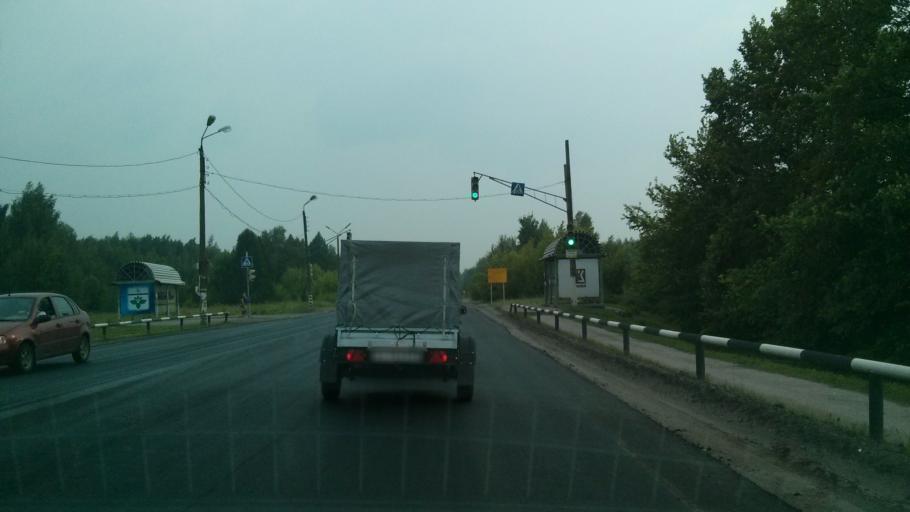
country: RU
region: Nizjnij Novgorod
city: Kstovo
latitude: 56.1141
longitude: 44.1497
